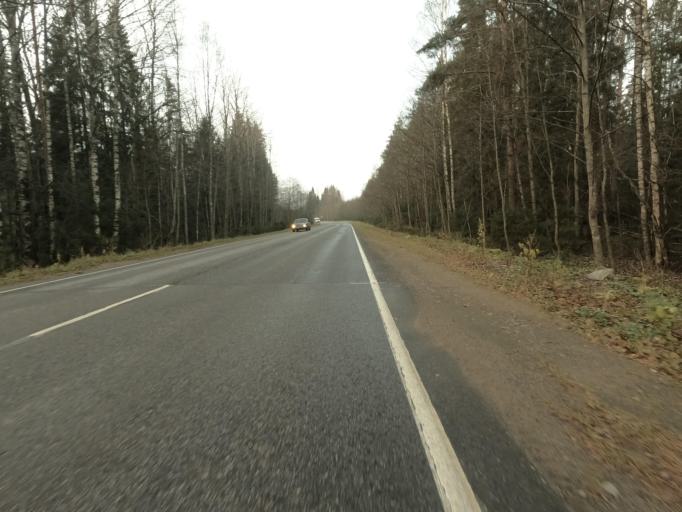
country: RU
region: Leningrad
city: Kirovsk
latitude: 59.8239
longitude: 30.9822
